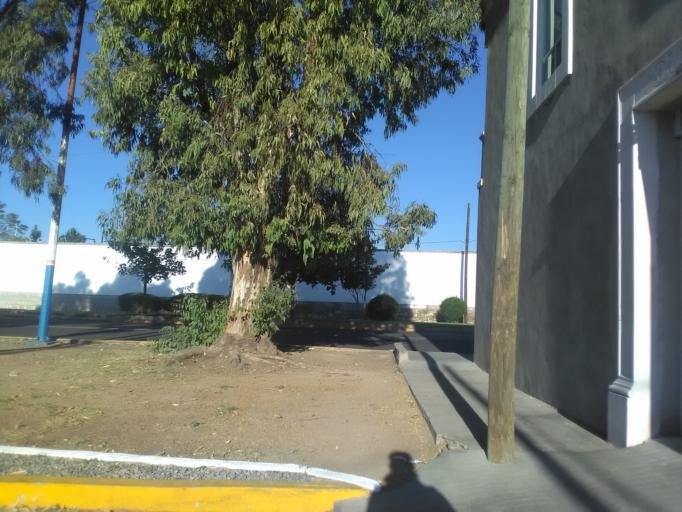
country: MX
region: Durango
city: Victoria de Durango
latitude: 24.0336
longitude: -104.6800
